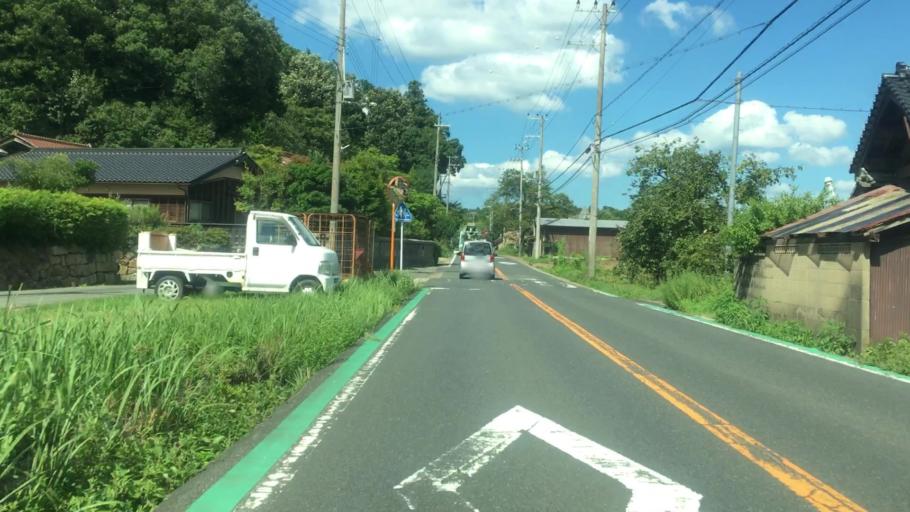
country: JP
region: Kyoto
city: Miyazu
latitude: 35.6103
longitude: 135.0531
